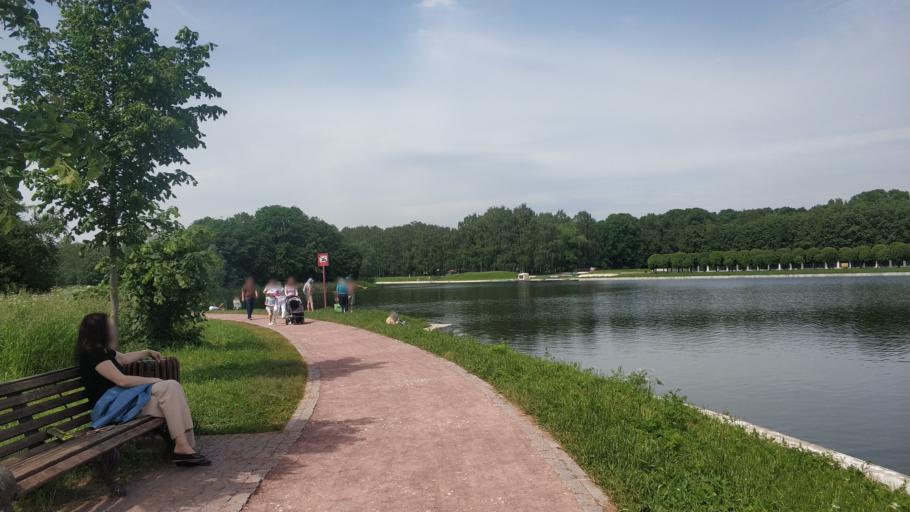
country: RU
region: Moscow
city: Perovo
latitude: 55.7337
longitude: 37.8053
